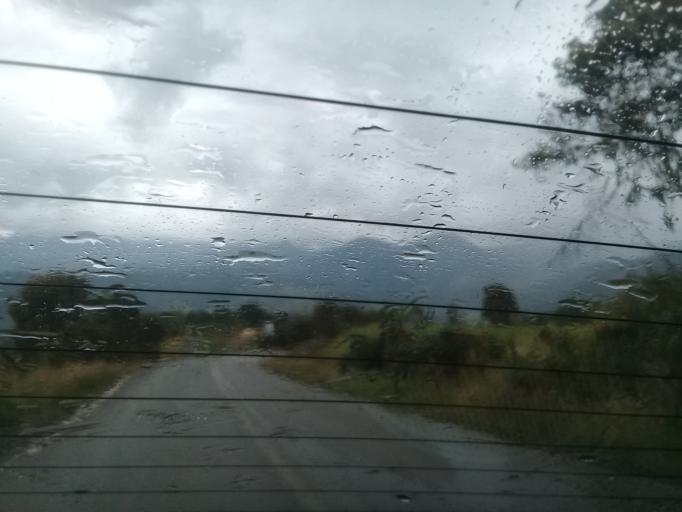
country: CO
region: Cundinamarca
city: Junin
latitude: 4.8363
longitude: -73.7587
